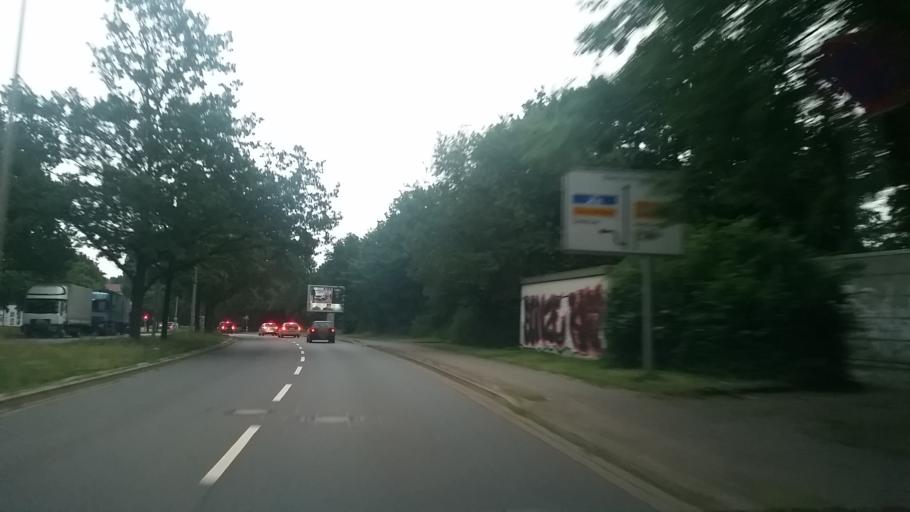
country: DE
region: Lower Saxony
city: Hemmingen
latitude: 52.3425
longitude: 9.6945
